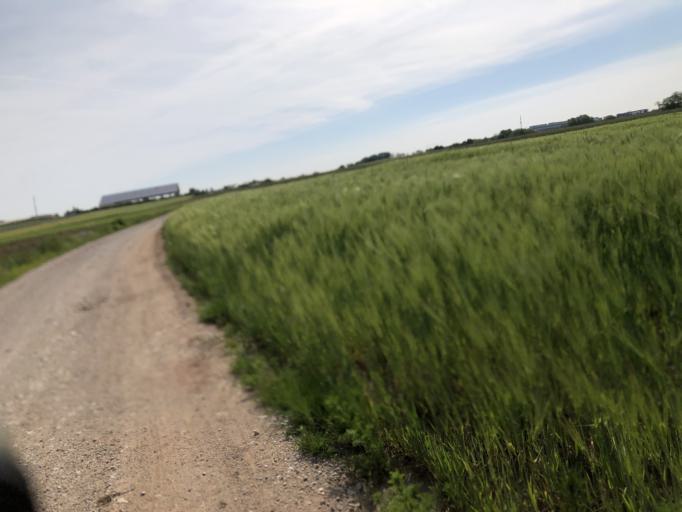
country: DE
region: Bavaria
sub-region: Regierungsbezirk Mittelfranken
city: Erlangen
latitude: 49.5506
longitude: 11.0032
